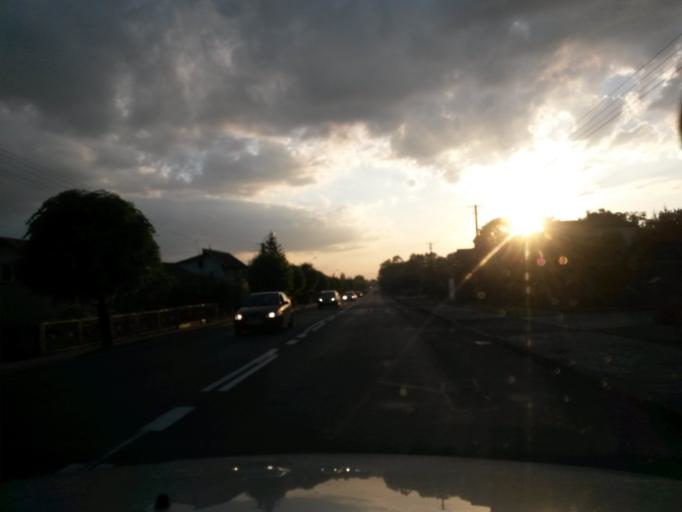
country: PL
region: Lodz Voivodeship
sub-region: Powiat wielunski
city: Mokrsko
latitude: 51.2622
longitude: 18.4699
